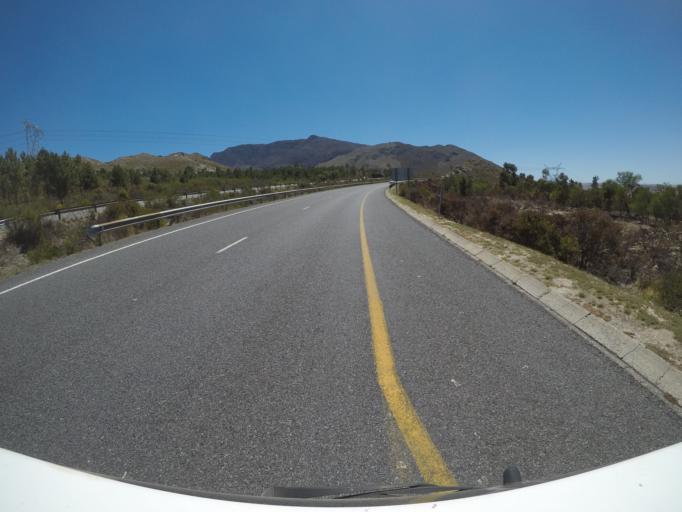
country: ZA
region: Western Cape
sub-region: Overberg District Municipality
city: Grabouw
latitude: -34.2225
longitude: 19.1880
